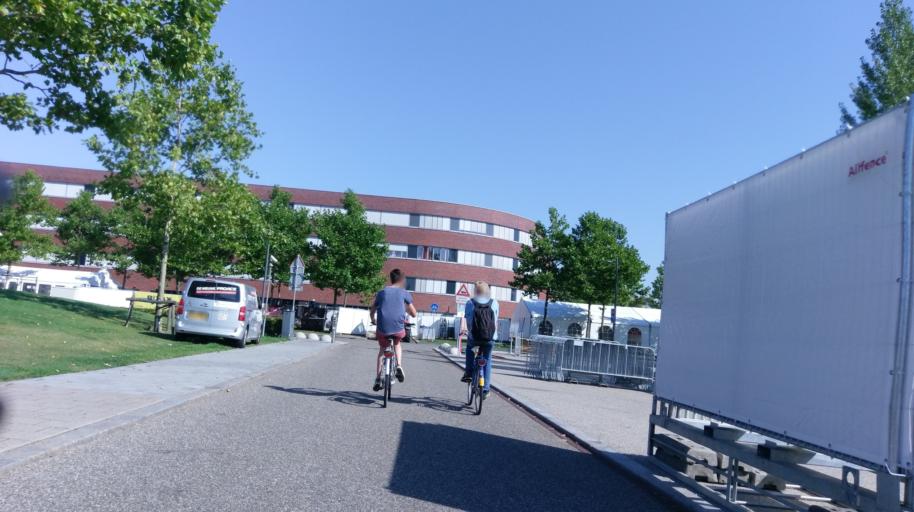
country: NL
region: Flevoland
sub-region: Gemeente Almere
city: Almere Stad
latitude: 52.3682
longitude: 5.2215
